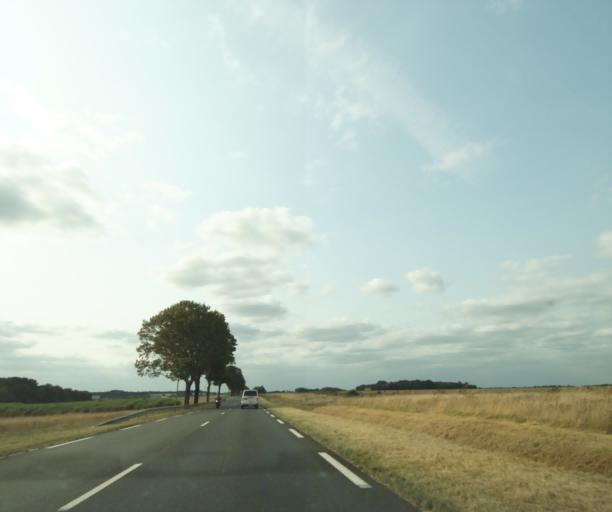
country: FR
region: Centre
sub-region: Departement d'Indre-et-Loire
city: Truyes
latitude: 47.2483
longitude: 0.8534
